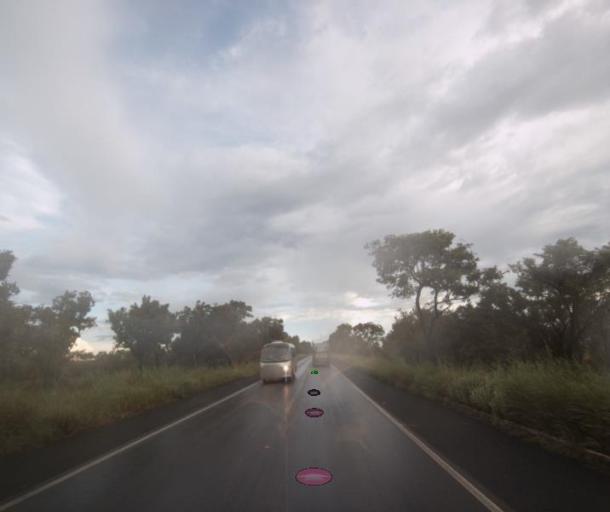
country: BR
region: Goias
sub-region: Porangatu
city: Porangatu
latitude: -13.8521
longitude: -49.0483
